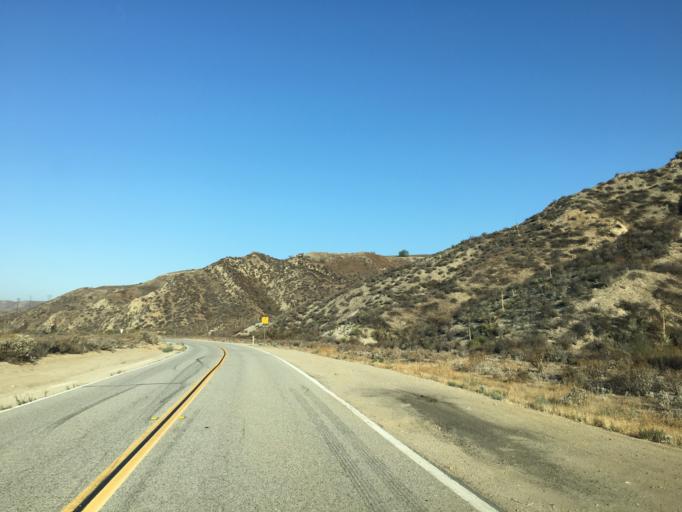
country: US
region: California
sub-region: Los Angeles County
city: Val Verde
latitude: 34.4274
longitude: -118.6354
